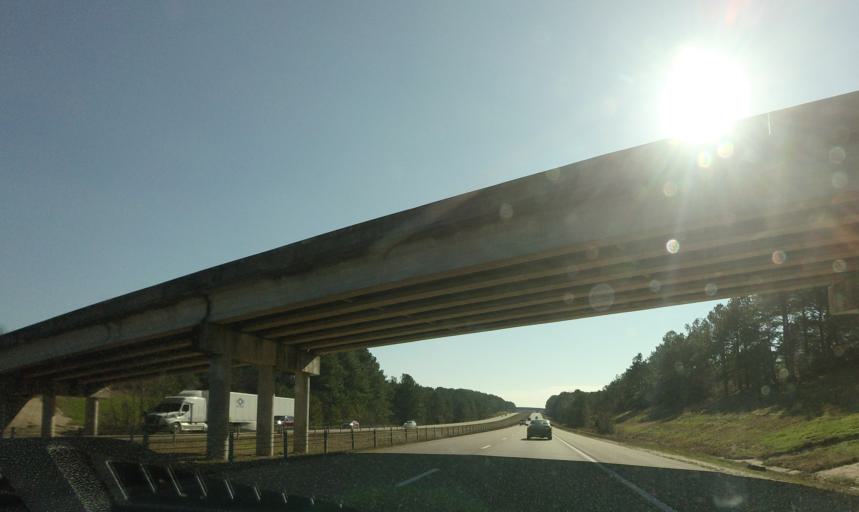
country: US
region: Mississippi
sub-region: Marshall County
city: Holly Springs
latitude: 34.7679
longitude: -89.4690
